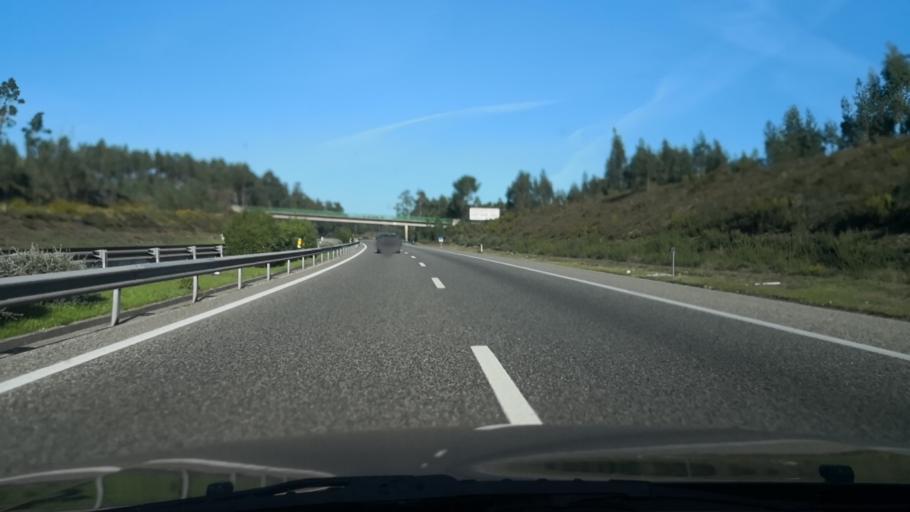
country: PT
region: Coimbra
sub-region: Soure
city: Soure
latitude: 39.9906
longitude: -8.6162
